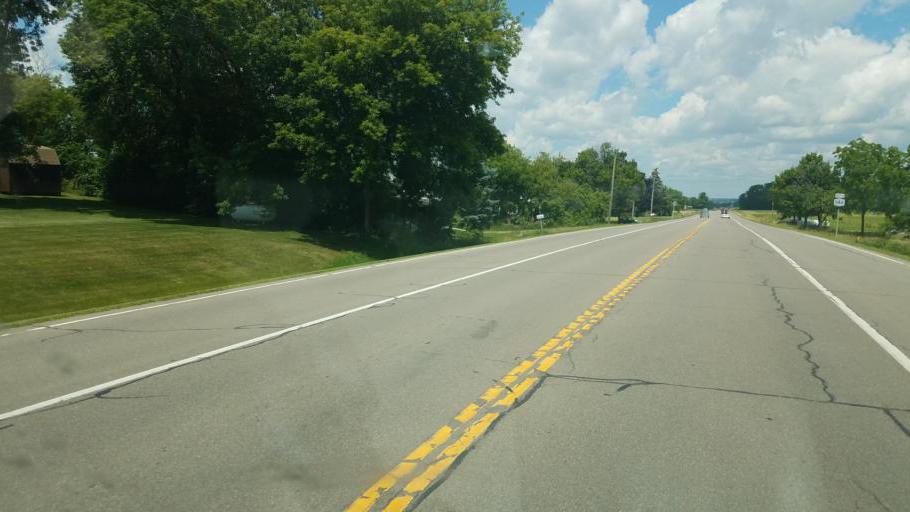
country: US
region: New York
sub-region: Yates County
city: Penn Yan
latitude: 42.6150
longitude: -77.0385
